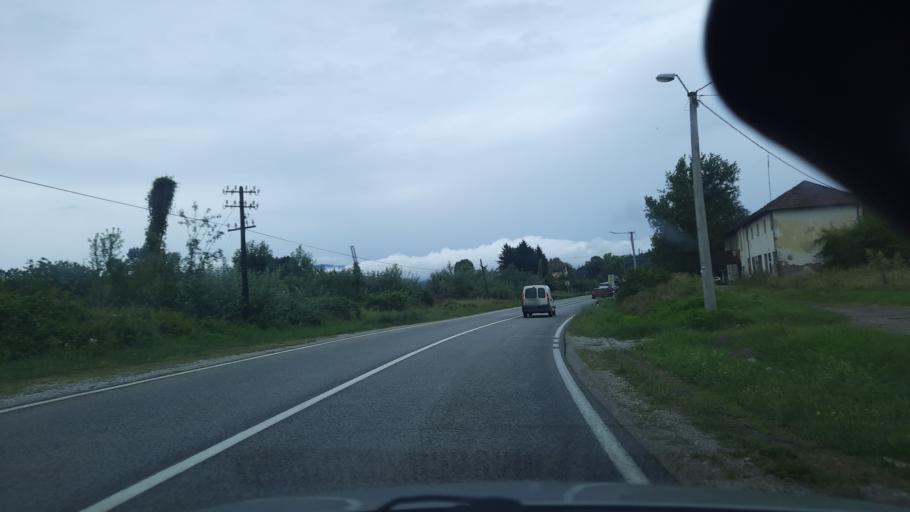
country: RS
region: Central Serbia
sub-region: Raski Okrug
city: Kraljevo
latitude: 43.7297
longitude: 20.8027
